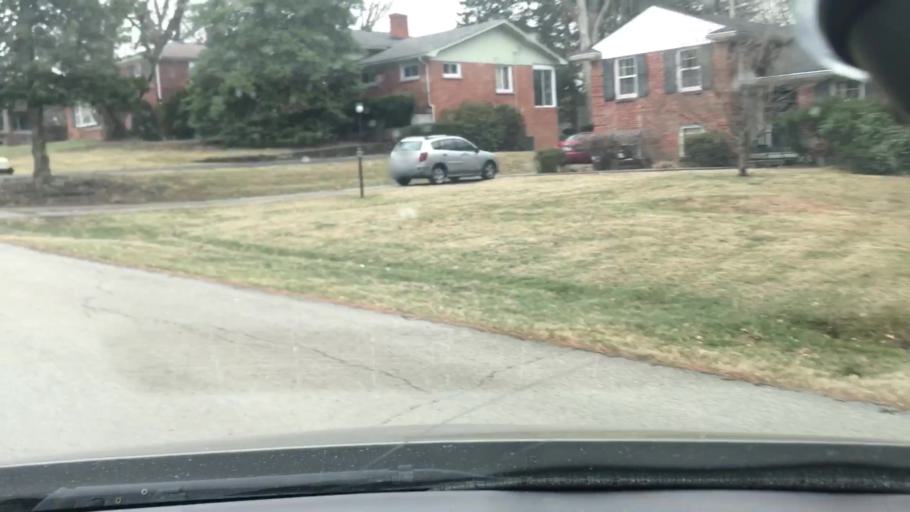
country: US
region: Kentucky
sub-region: Jefferson County
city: Barbourmeade
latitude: 38.2968
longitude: -85.6046
